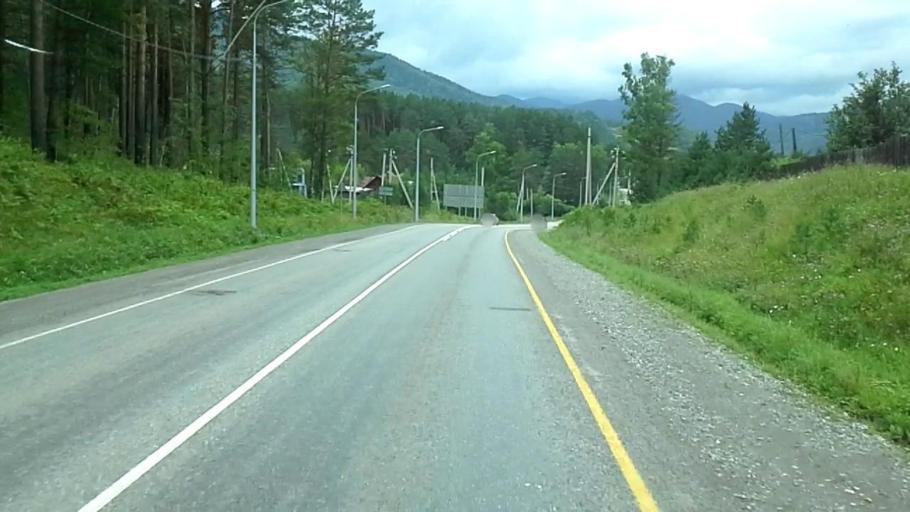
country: RU
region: Altay
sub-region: Mayminskiy Rayon
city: Manzherok
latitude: 51.8203
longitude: 85.7846
